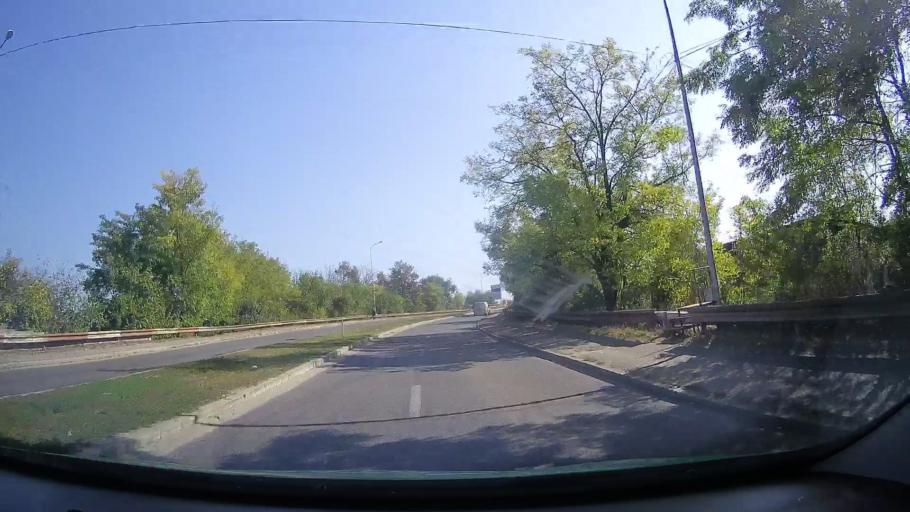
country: RO
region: Arad
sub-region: Oras Lipova
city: Radna
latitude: 46.0929
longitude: 21.6859
